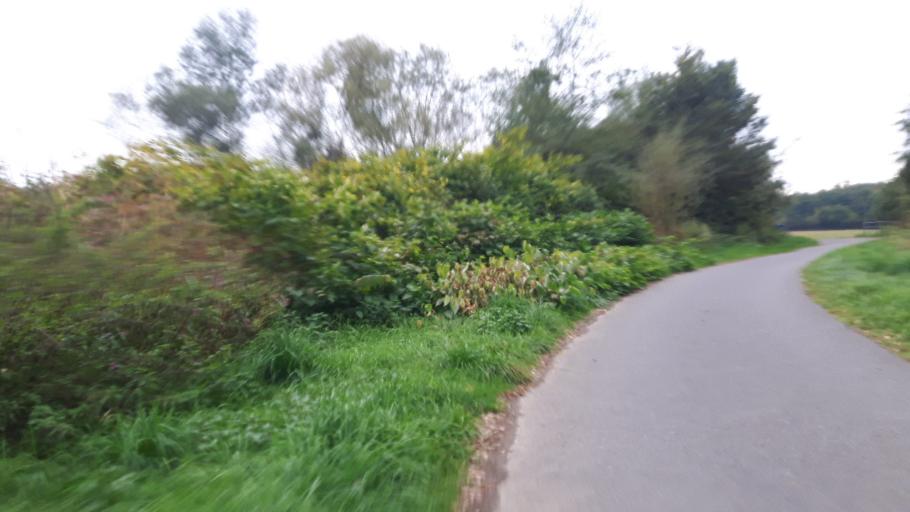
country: DE
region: North Rhine-Westphalia
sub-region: Regierungsbezirk Koln
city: Hennef
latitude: 50.7770
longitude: 7.3176
